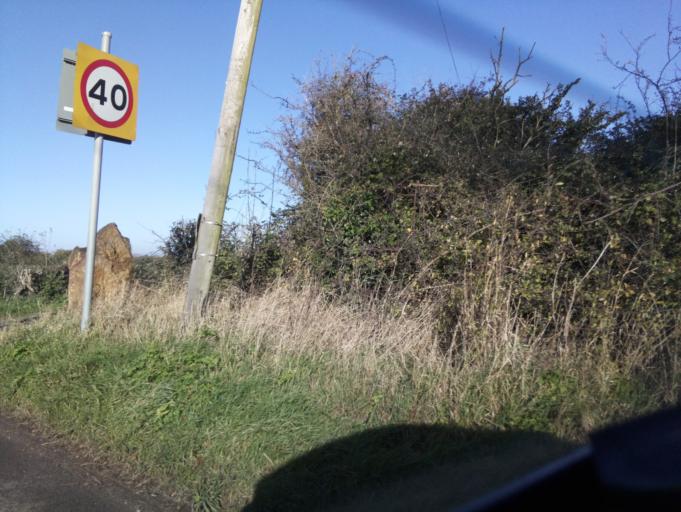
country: GB
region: England
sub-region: Somerset
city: Stoke-sub-Hamdon
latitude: 50.9719
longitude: -2.7188
